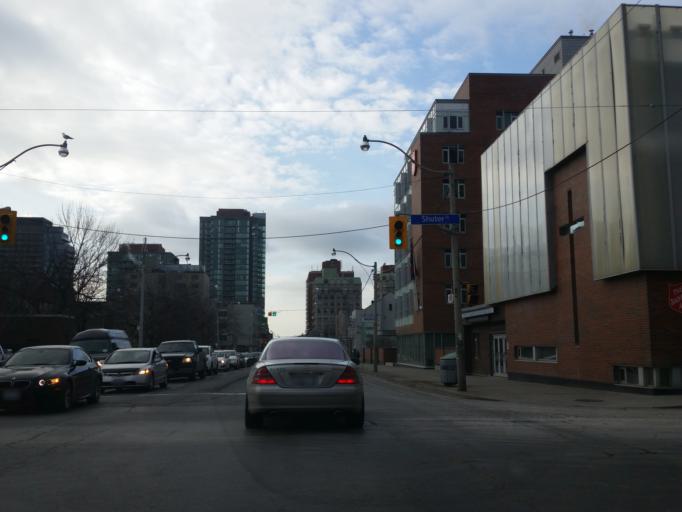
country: CA
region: Ontario
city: Toronto
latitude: 43.6554
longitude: -79.3740
